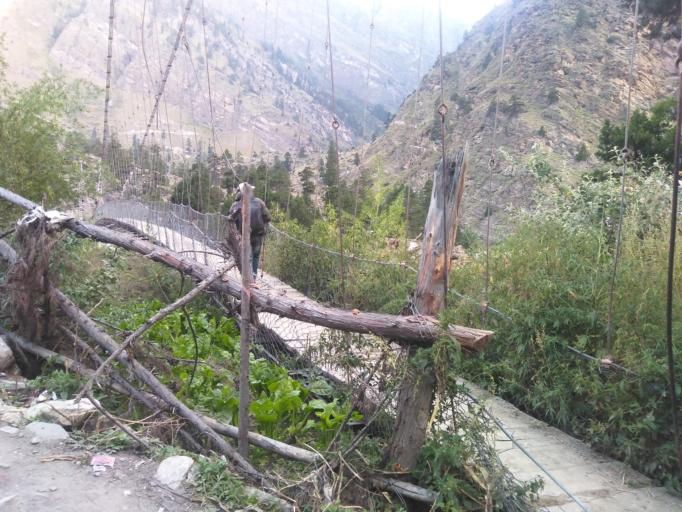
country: NP
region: Western Region
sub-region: Dhawalagiri Zone
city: Jomsom
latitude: 28.8948
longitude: 83.0357
